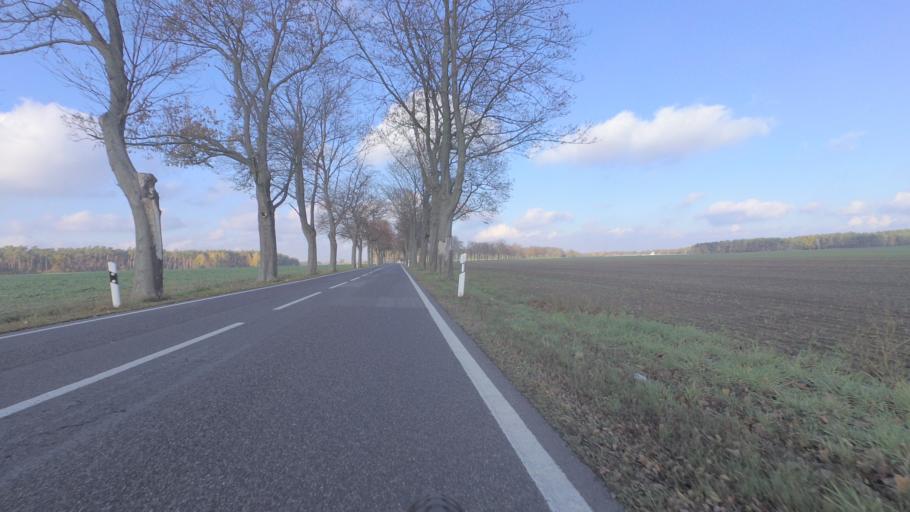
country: DE
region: Brandenburg
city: Rangsdorf
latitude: 52.2584
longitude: 13.3432
